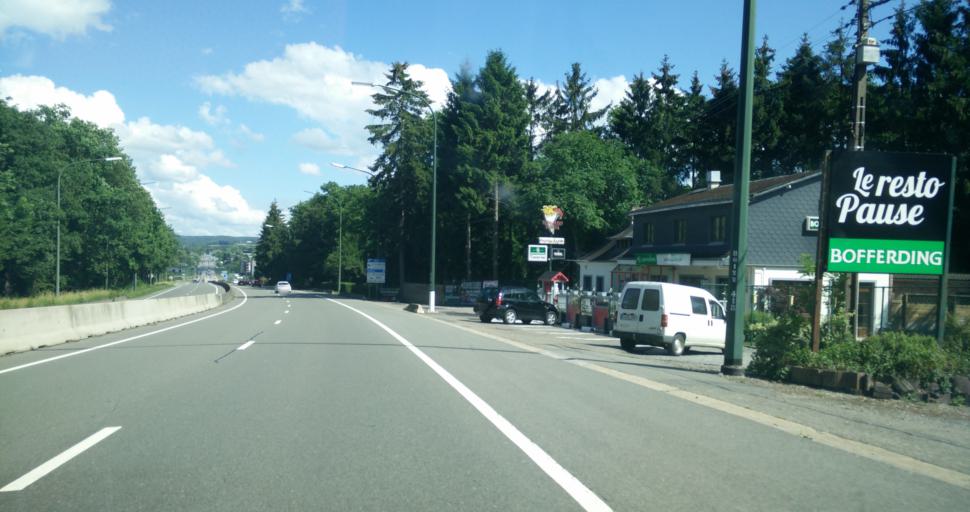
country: BE
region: Wallonia
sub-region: Province du Luxembourg
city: Marche-en-Famenne
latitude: 50.2351
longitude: 5.3024
